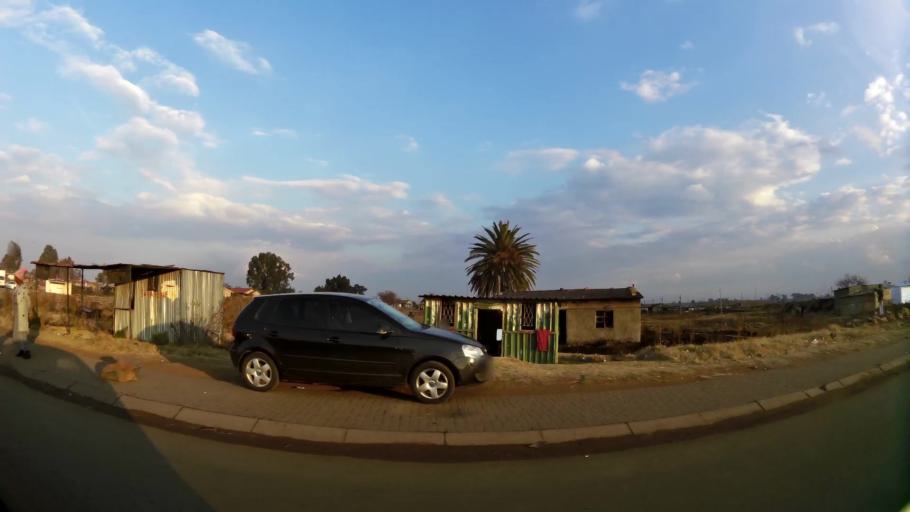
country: ZA
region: Gauteng
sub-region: City of Johannesburg Metropolitan Municipality
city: Orange Farm
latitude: -26.5349
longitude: 27.8454
